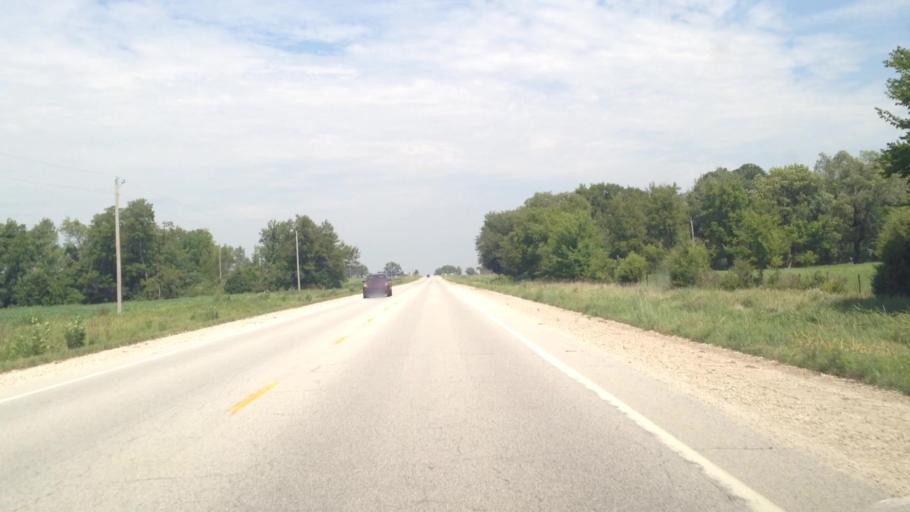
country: US
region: Kansas
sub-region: Neosho County
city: Erie
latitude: 37.4660
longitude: -95.2695
